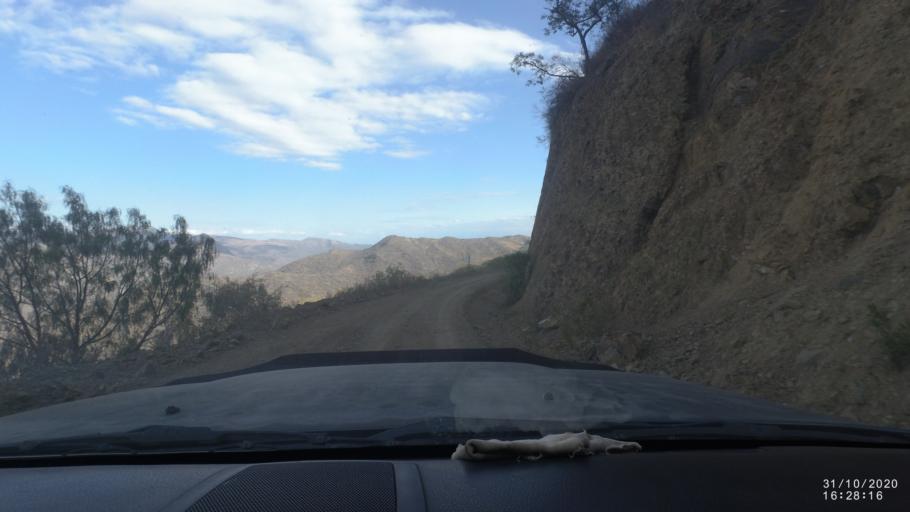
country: BO
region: Chuquisaca
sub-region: Provincia Zudanez
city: Mojocoya
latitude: -18.4114
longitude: -64.5865
